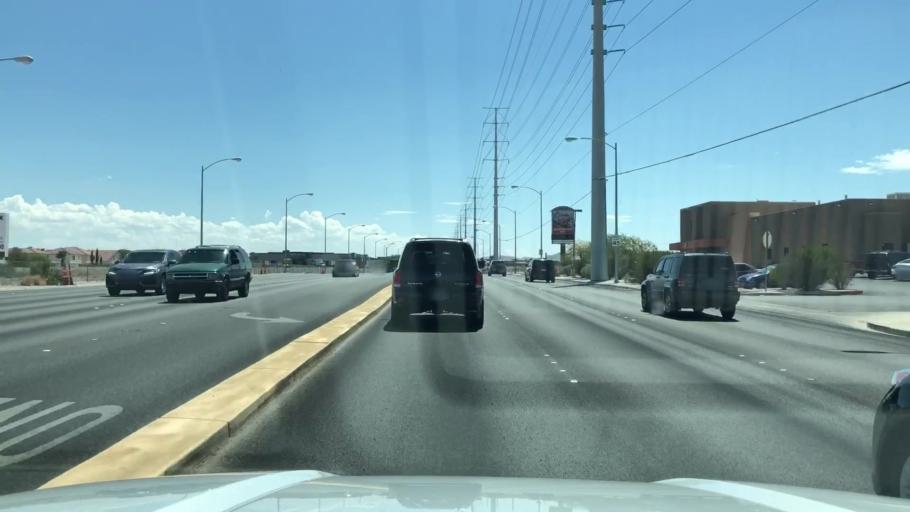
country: US
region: Nevada
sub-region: Clark County
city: Spring Valley
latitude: 36.0844
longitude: -115.2793
